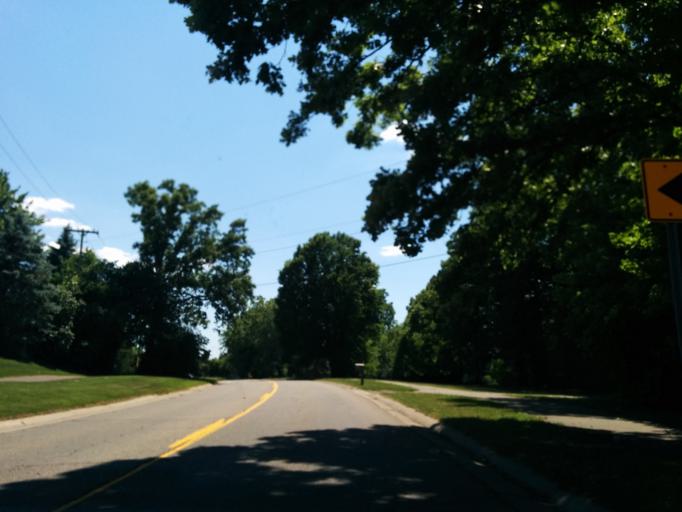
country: US
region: Michigan
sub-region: Oakland County
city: West Bloomfield Township
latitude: 42.5494
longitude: -83.3796
